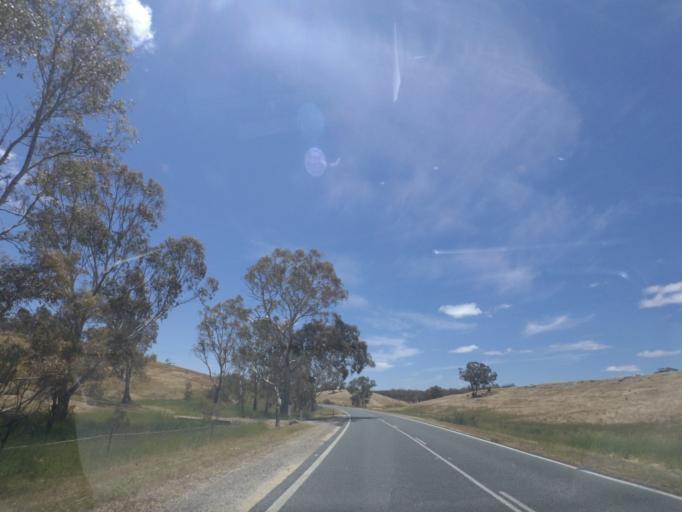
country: AU
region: Victoria
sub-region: Mount Alexander
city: Castlemaine
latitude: -37.1925
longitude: 144.1487
